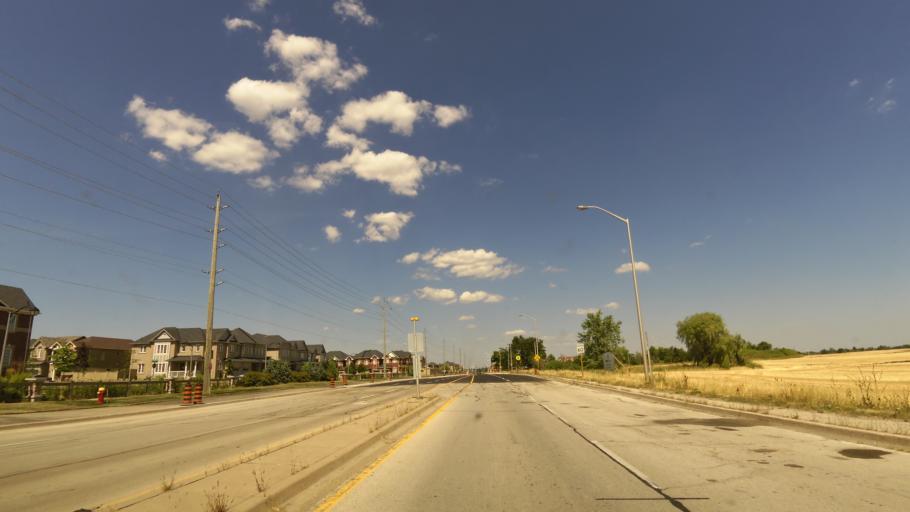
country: CA
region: Ontario
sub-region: Halton
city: Milton
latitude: 43.6281
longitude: -79.8728
